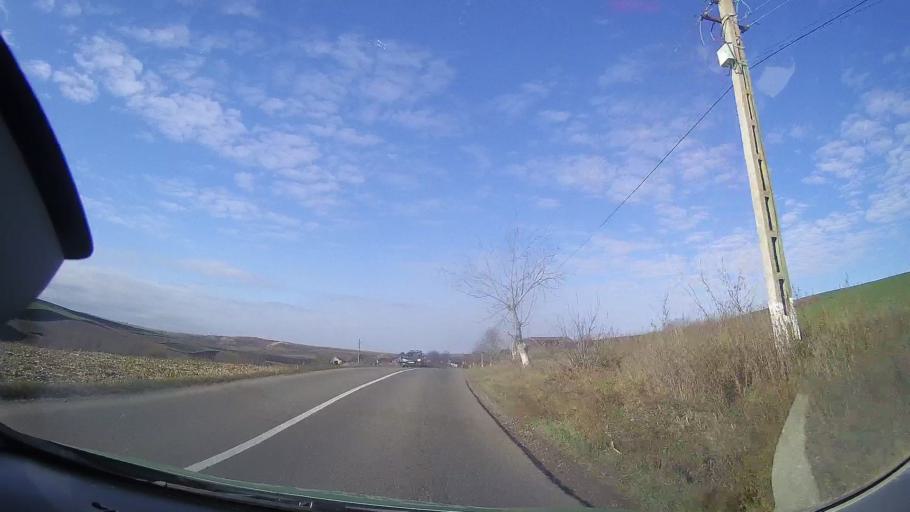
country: RO
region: Mures
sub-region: Comuna Grebenisu de Campie
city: Grebenisu de Campie
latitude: 46.6074
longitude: 24.2687
